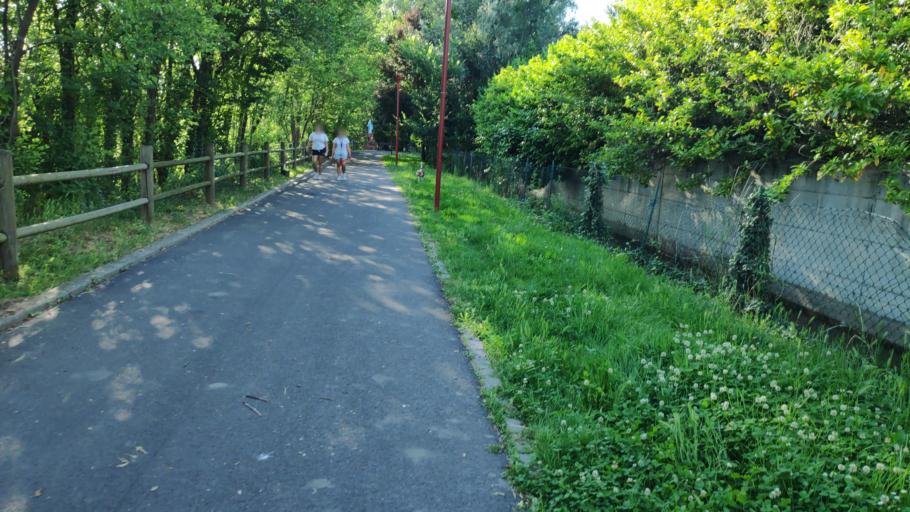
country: IT
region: Lombardy
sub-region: Citta metropolitana di Milano
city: Basiglio
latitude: 45.3526
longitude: 9.1629
